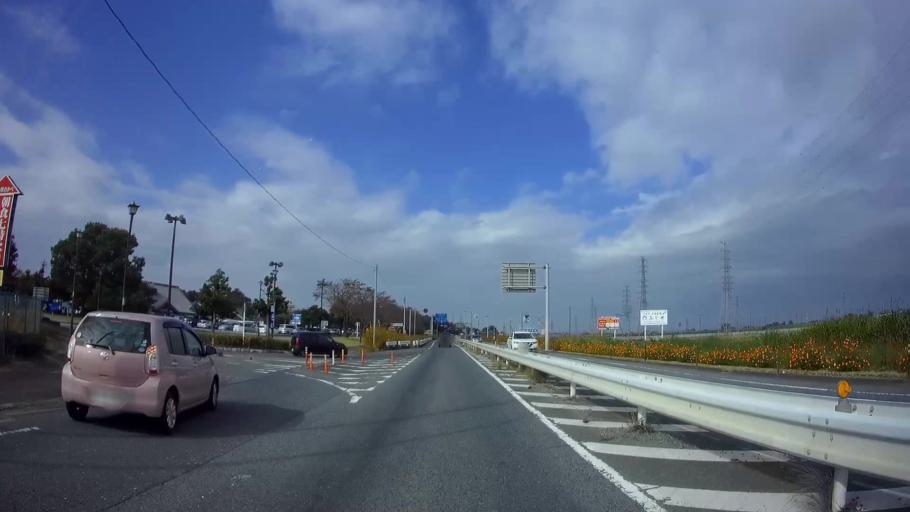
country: JP
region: Saitama
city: Fukayacho
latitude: 36.2191
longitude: 139.2425
